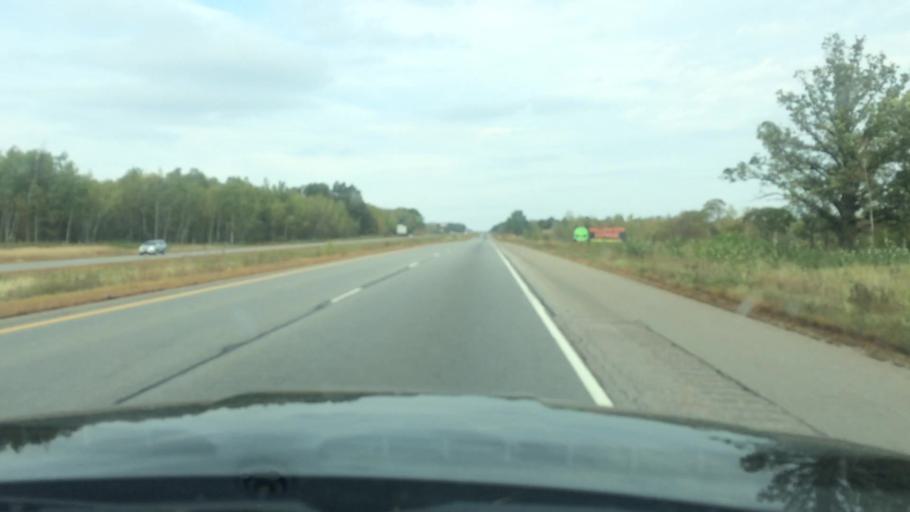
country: US
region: Wisconsin
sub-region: Marathon County
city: Mosinee
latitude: 44.7445
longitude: -89.6796
